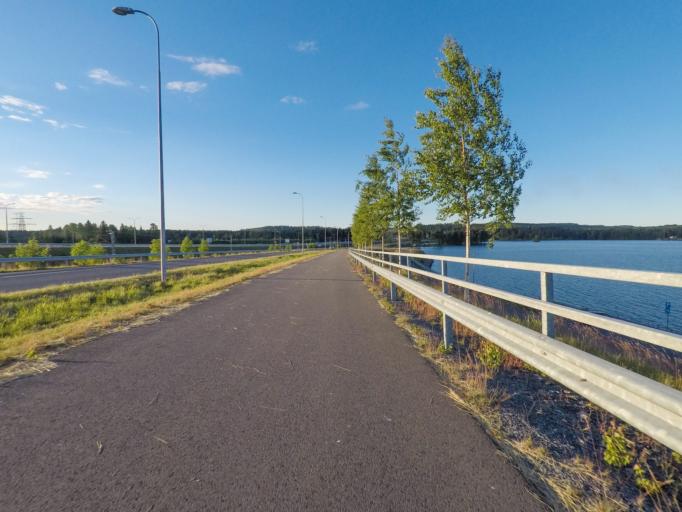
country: FI
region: Northern Savo
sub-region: Kuopio
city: Kuopio
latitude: 62.9487
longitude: 27.6757
